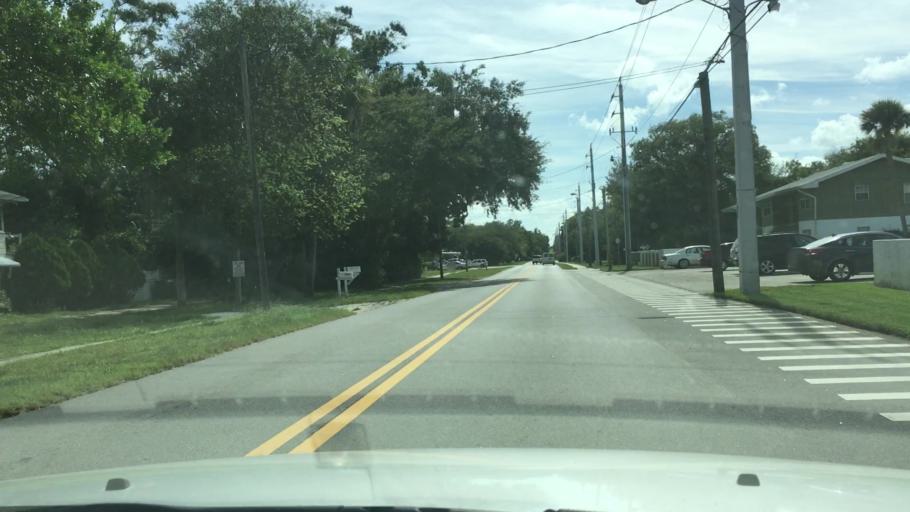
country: US
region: Florida
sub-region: Volusia County
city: Holly Hill
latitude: 29.2372
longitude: -81.0475
